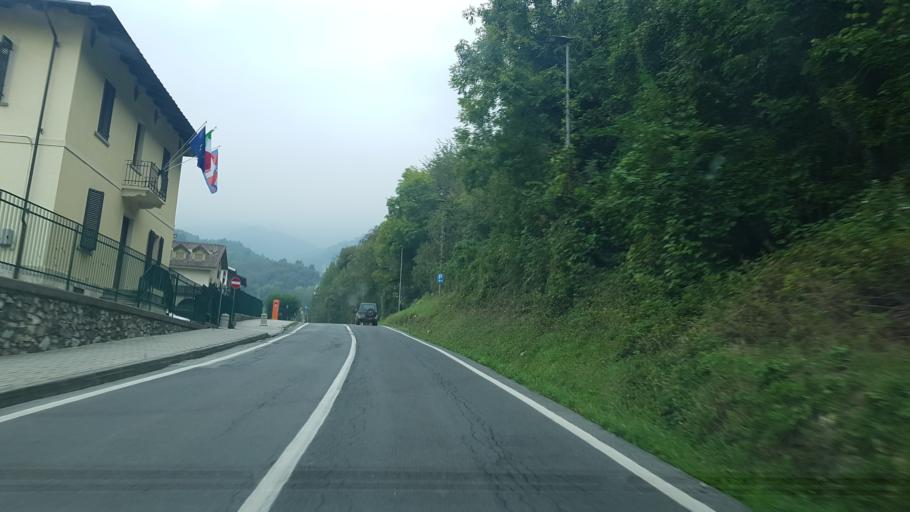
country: IT
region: Piedmont
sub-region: Provincia di Cuneo
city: Frabosa Sottana
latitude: 44.3063
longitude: 7.8009
